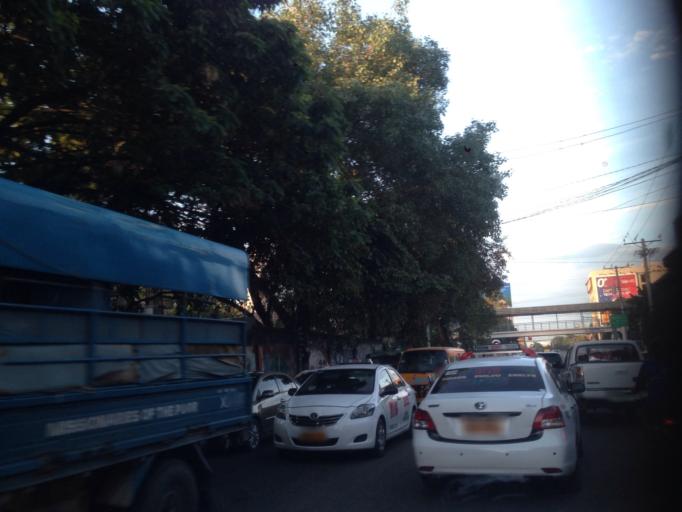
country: PH
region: Central Visayas
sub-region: Cebu City
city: Baugo
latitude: 10.3135
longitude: 123.9132
